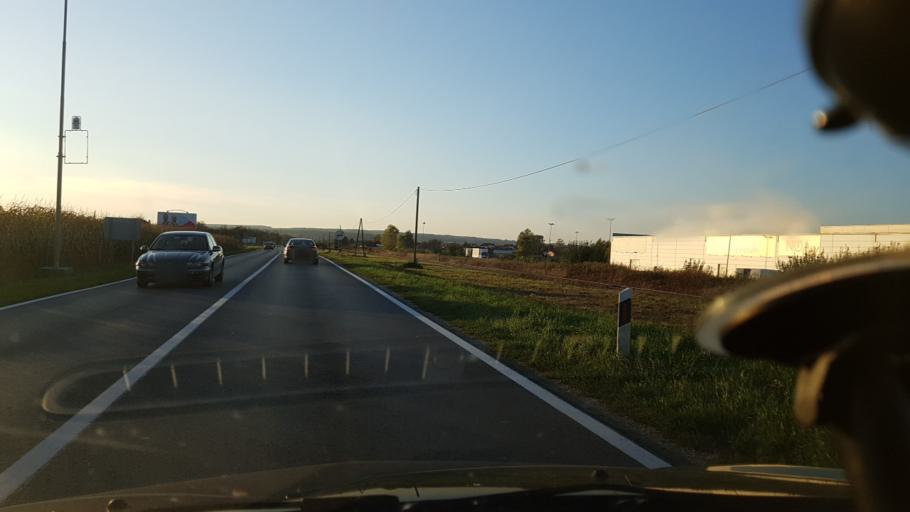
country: HR
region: Koprivnicko-Krizevacka
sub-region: Grad Koprivnica
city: Koprivnica
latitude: 46.1427
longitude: 16.8346
